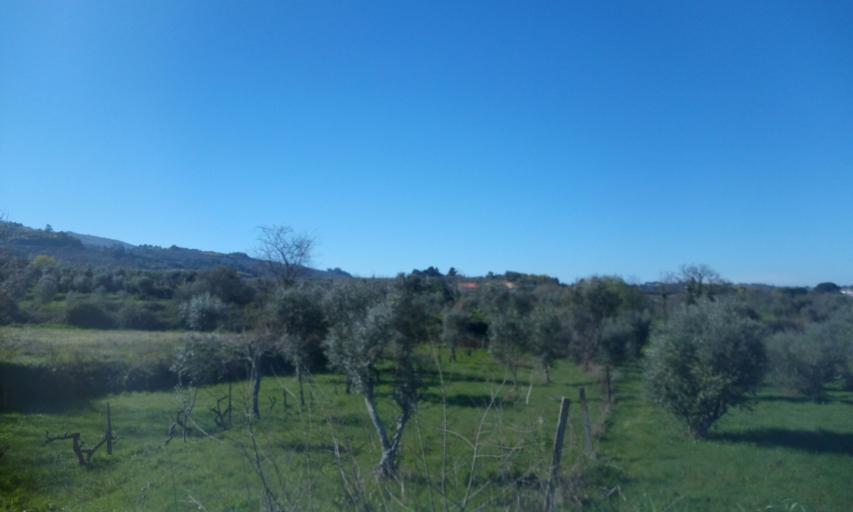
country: PT
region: Guarda
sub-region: Fornos de Algodres
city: Fornos de Algodres
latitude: 40.5252
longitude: -7.5575
